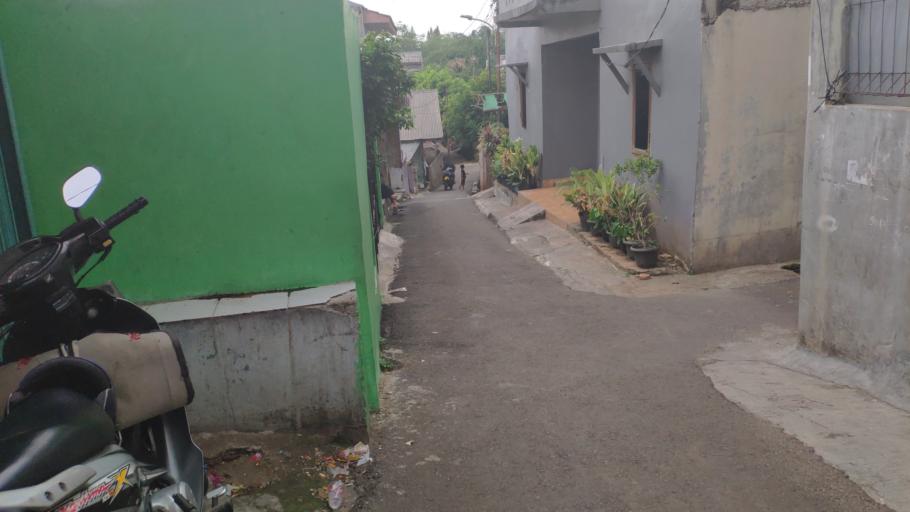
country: ID
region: Jakarta Raya
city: Jakarta
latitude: -6.2719
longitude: 106.8296
